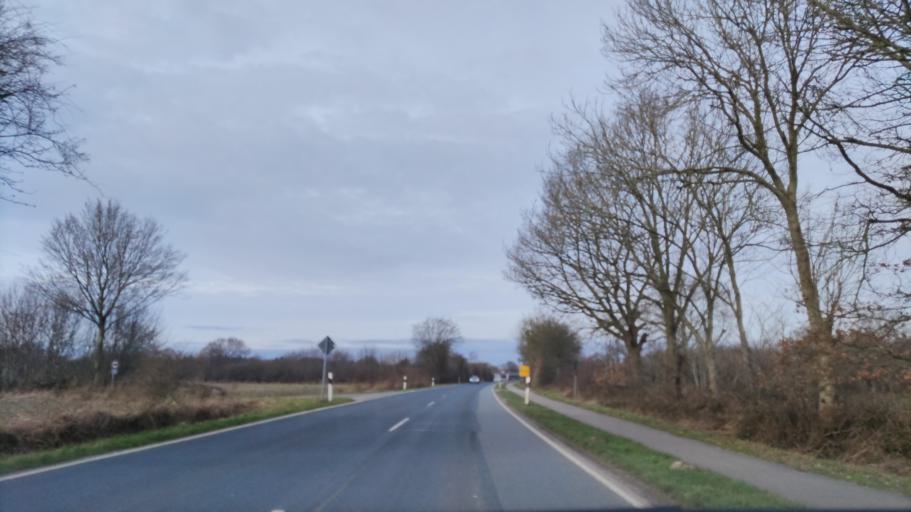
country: DE
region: Schleswig-Holstein
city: Busdorf
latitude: 54.4870
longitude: 9.5592
